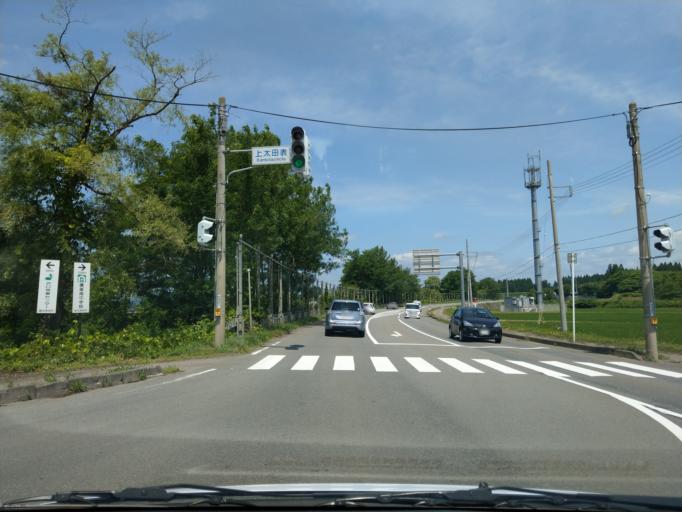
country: JP
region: Akita
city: Takanosu
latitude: 40.1952
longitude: 140.3968
